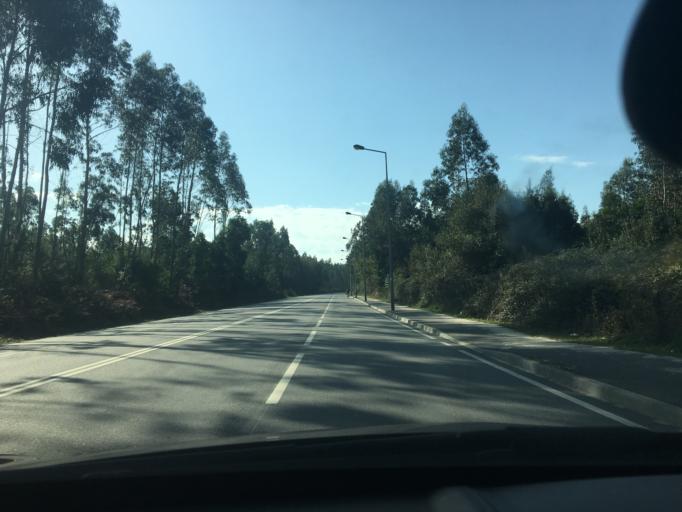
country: PT
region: Porto
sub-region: Maia
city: Anta
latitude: 41.2585
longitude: -8.6254
